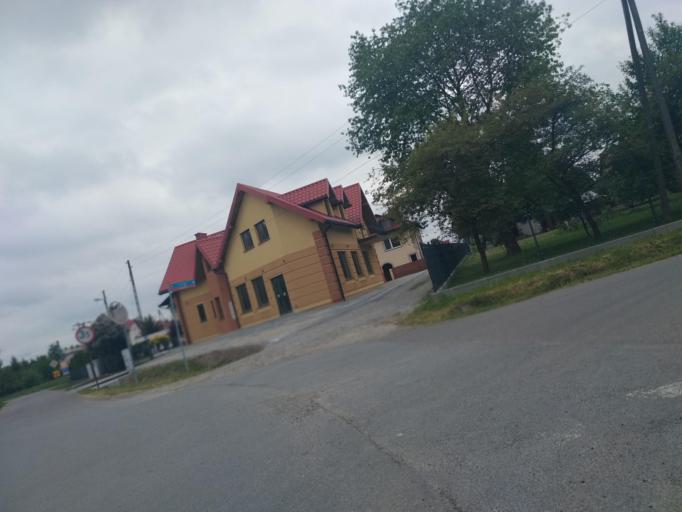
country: PL
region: Subcarpathian Voivodeship
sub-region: Krosno
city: Krosno
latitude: 49.6711
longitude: 21.7448
